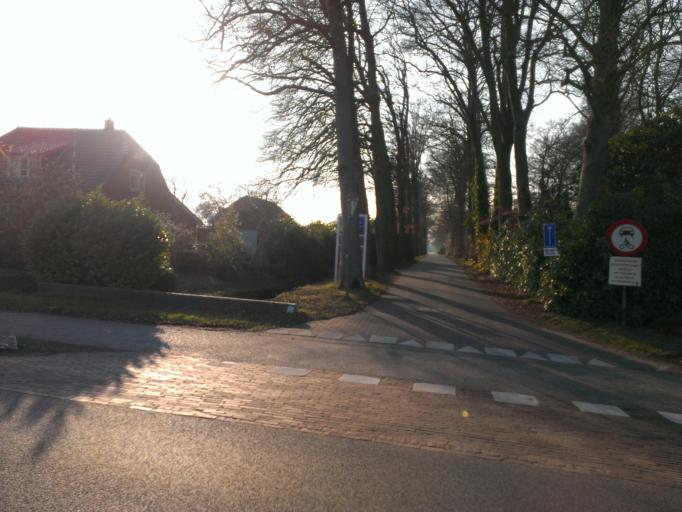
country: NL
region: Gelderland
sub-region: Gemeente Heerde
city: Heerde
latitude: 52.3959
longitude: 6.0330
